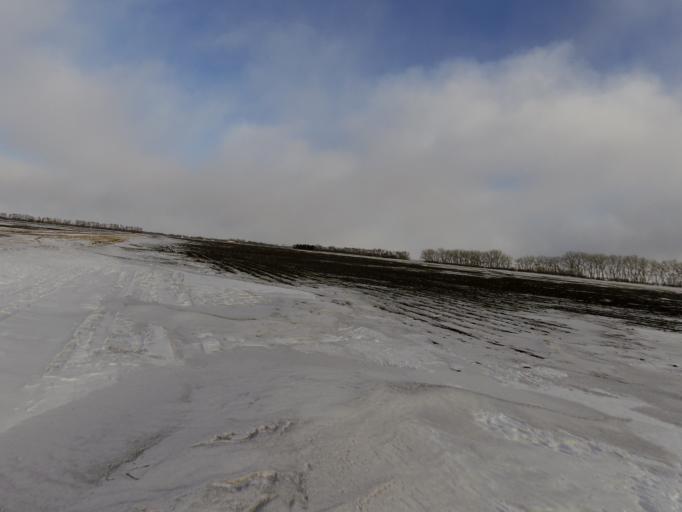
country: US
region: North Dakota
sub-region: Walsh County
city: Grafton
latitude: 48.3975
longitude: -97.2099
